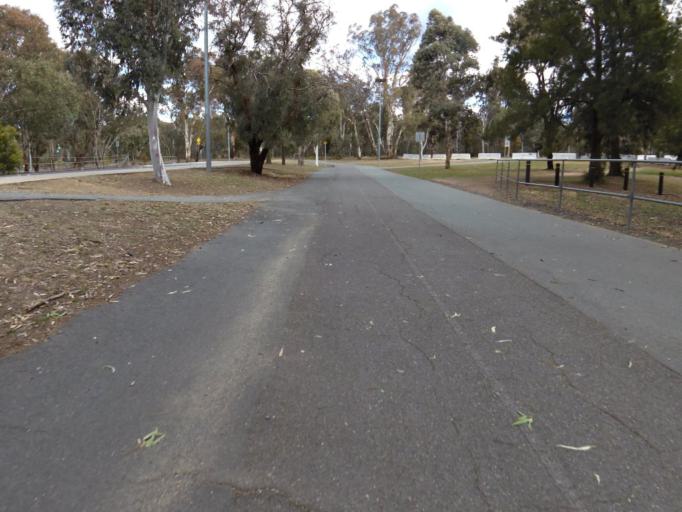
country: AU
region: Australian Capital Territory
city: Acton
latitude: -35.2501
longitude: 149.1049
